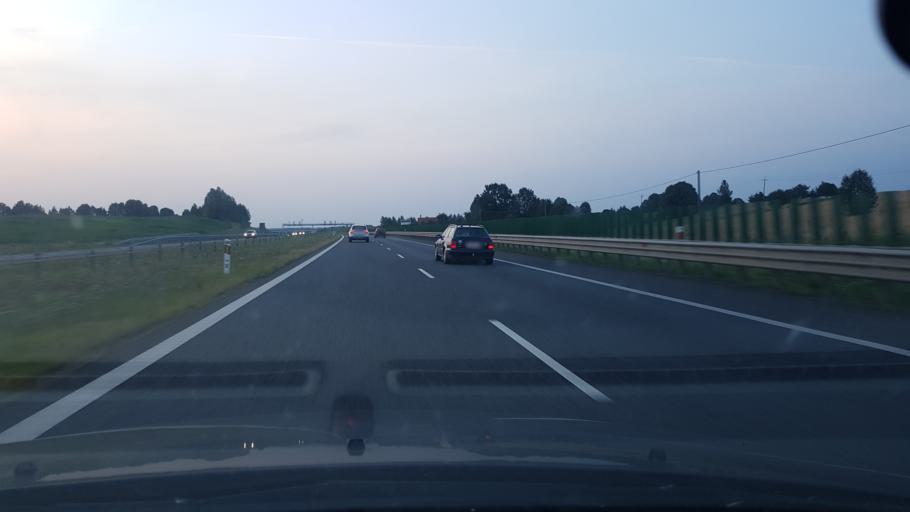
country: PL
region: Warmian-Masurian Voivodeship
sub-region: Powiat olsztynski
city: Olsztynek
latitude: 53.4824
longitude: 20.3212
